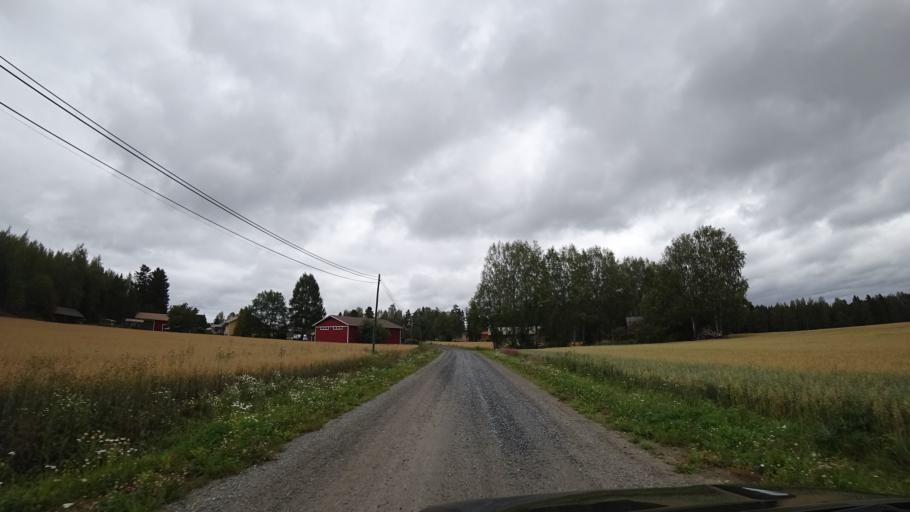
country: FI
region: Haeme
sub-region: Haemeenlinna
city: Lammi
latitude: 61.1298
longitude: 24.9871
